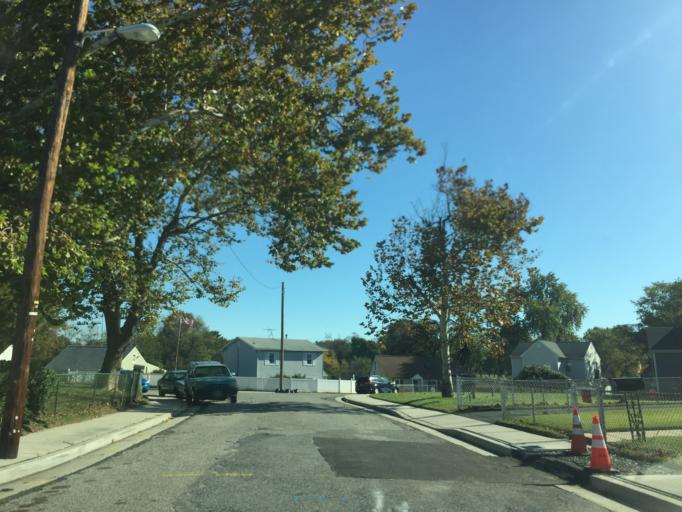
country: US
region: Maryland
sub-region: Baltimore County
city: Dundalk
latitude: 39.2524
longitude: -76.5089
